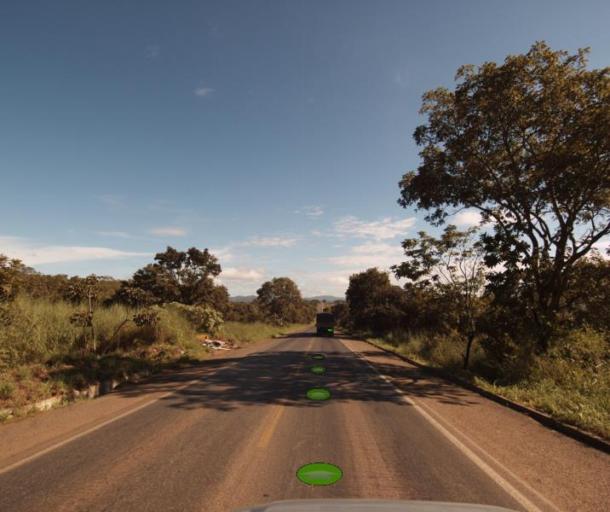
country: BR
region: Goias
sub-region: Uruacu
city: Uruacu
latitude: -14.5567
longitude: -49.1581
